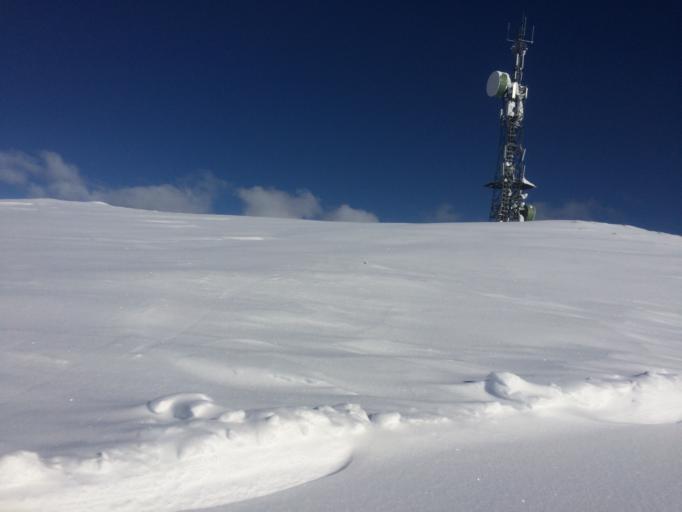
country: NO
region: Oppland
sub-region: Gausdal
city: Segalstad bru
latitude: 61.3508
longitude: 10.0866
